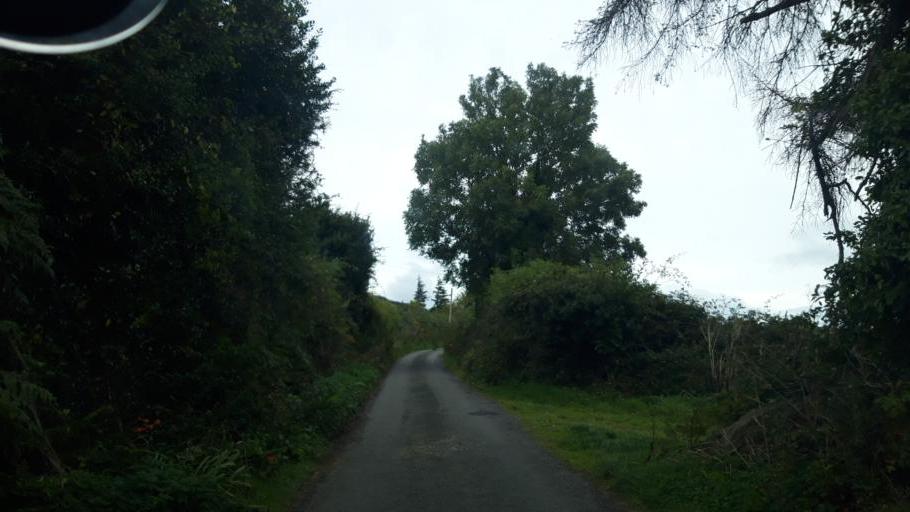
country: IE
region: Leinster
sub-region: Wicklow
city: Enniskerry
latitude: 53.1756
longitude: -6.2113
